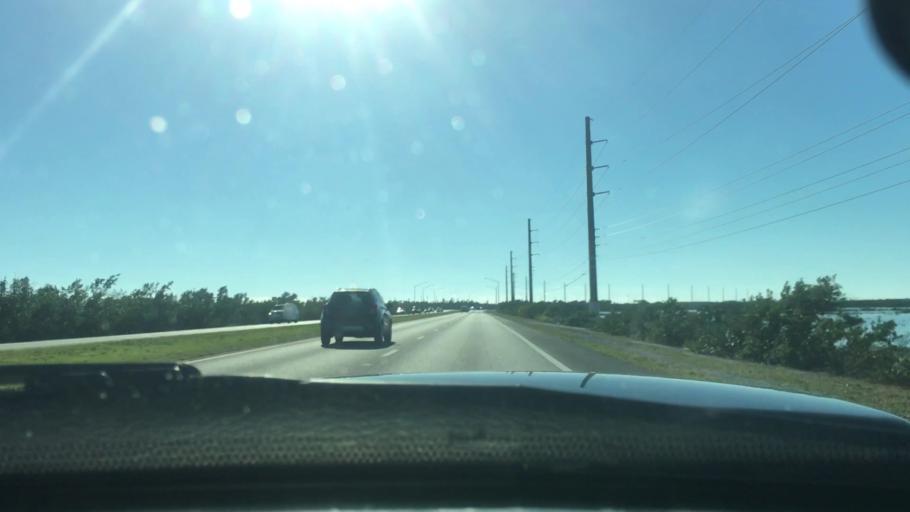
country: US
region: Florida
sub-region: Monroe County
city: Stock Island
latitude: 24.5830
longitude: -81.7030
